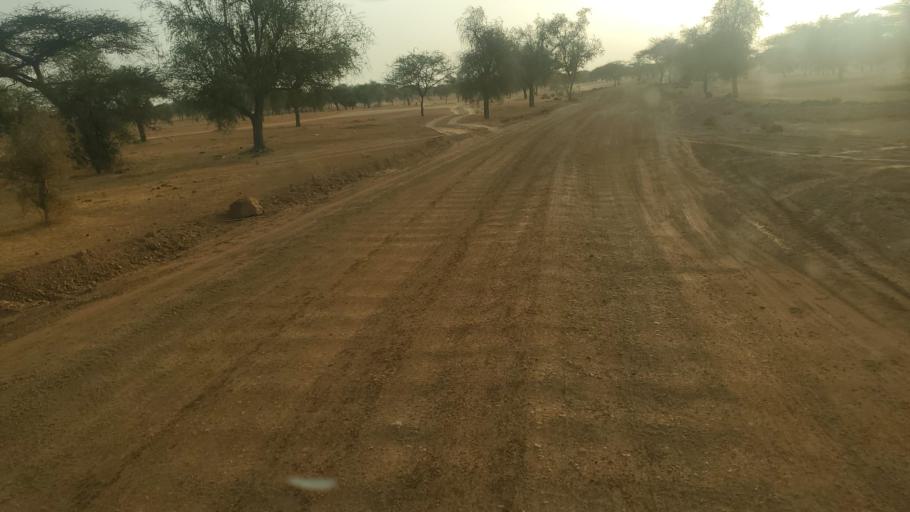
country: SN
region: Louga
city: Dara
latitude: 15.3654
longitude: -15.5604
